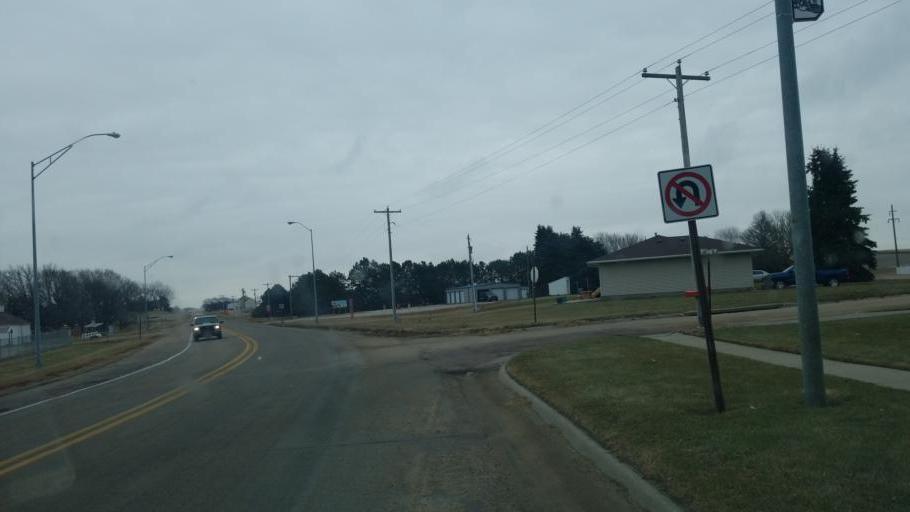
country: US
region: Nebraska
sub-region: Knox County
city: Bloomfield
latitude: 42.5977
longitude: -97.6374
